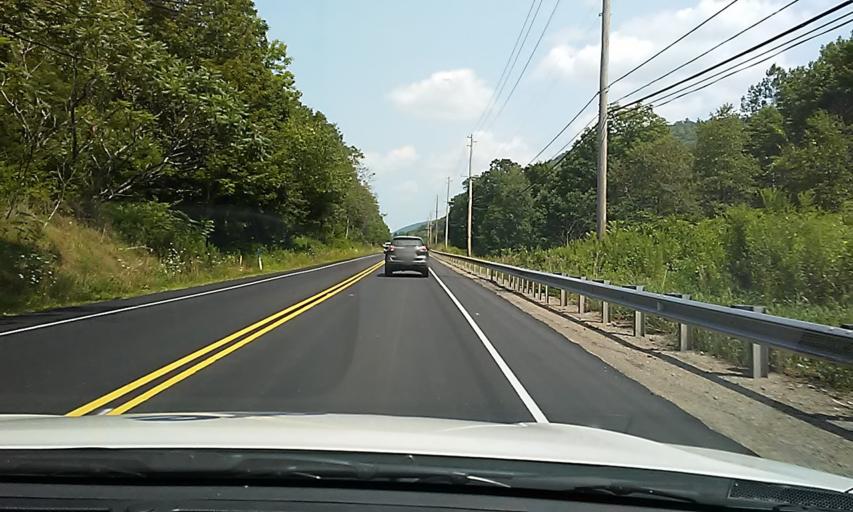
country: US
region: Pennsylvania
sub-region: Cameron County
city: Emporium
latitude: 41.4832
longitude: -78.3167
